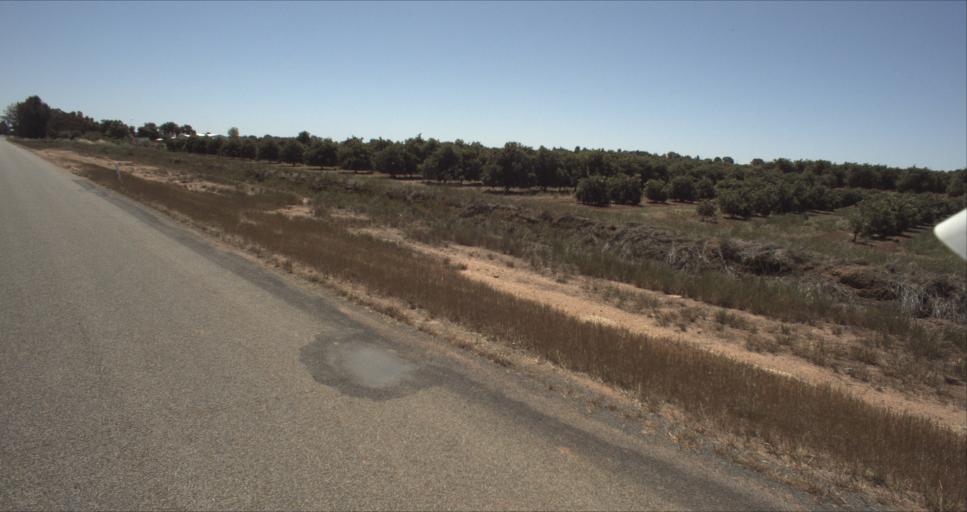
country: AU
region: New South Wales
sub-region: Leeton
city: Leeton
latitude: -34.5412
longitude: 146.3633
